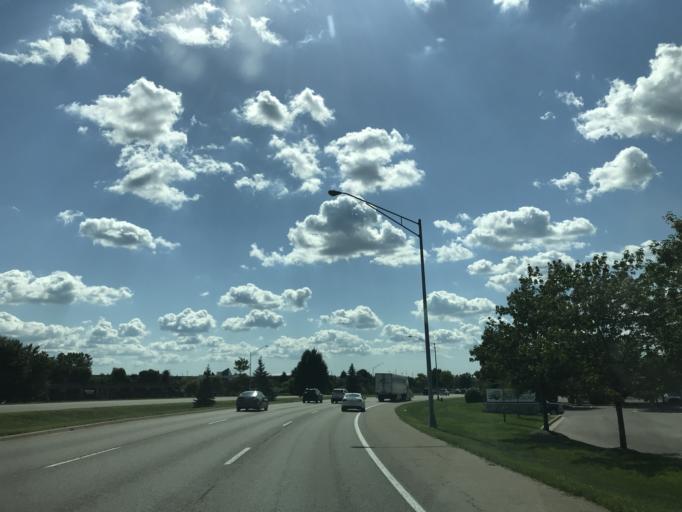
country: US
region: Michigan
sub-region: Kent County
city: Grandville
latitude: 42.8825
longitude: -85.7507
